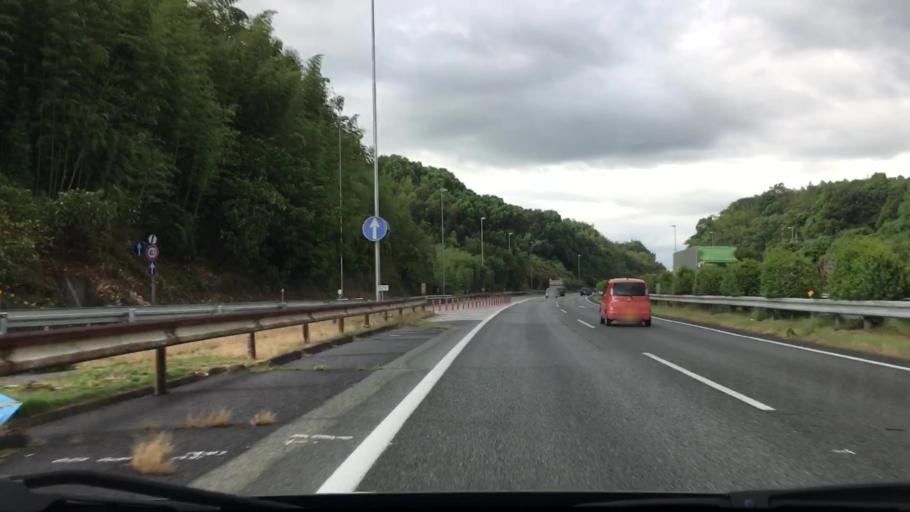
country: JP
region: Fukuoka
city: Koga
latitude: 33.7194
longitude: 130.4939
